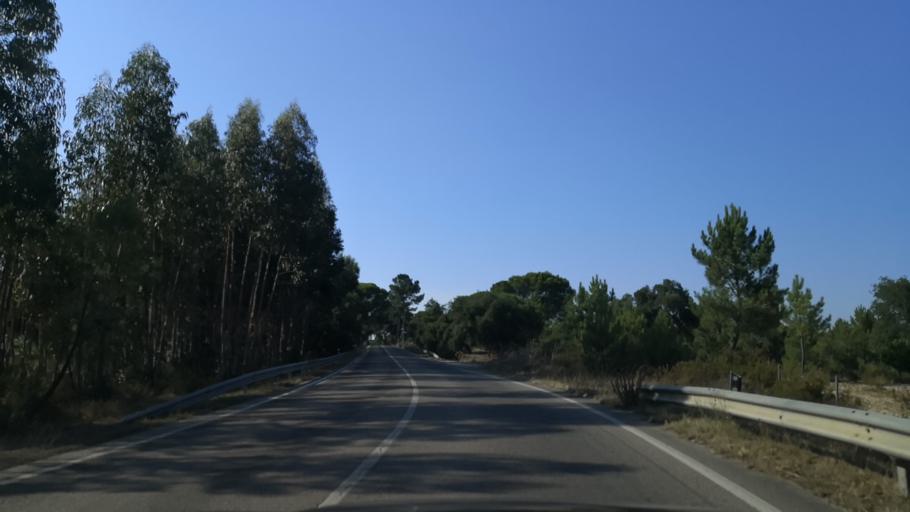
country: PT
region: Santarem
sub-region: Coruche
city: Coruche
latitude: 38.9733
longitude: -8.5387
